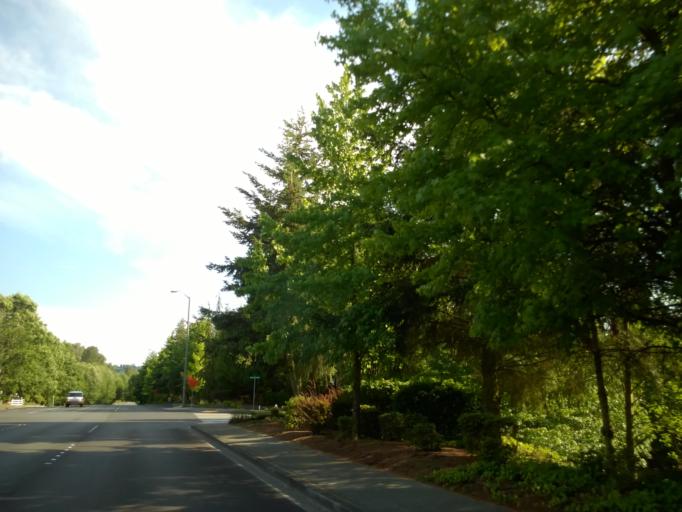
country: US
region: Washington
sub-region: King County
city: Bothell
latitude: 47.7782
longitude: -122.1815
